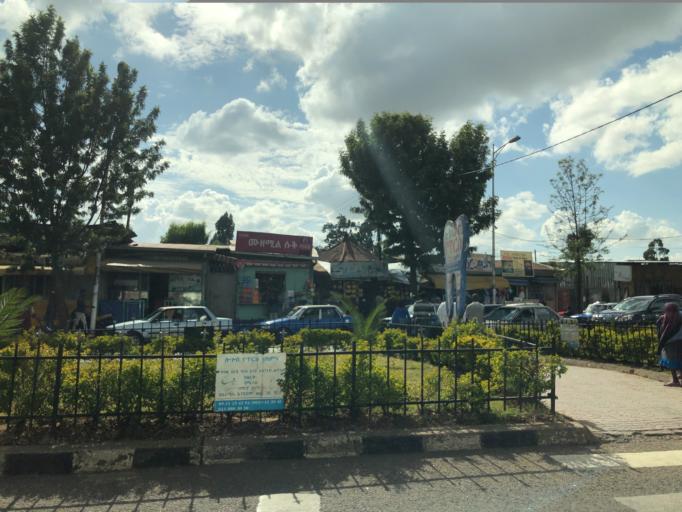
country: ET
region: Adis Abeba
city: Addis Ababa
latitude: 9.0266
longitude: 38.7758
